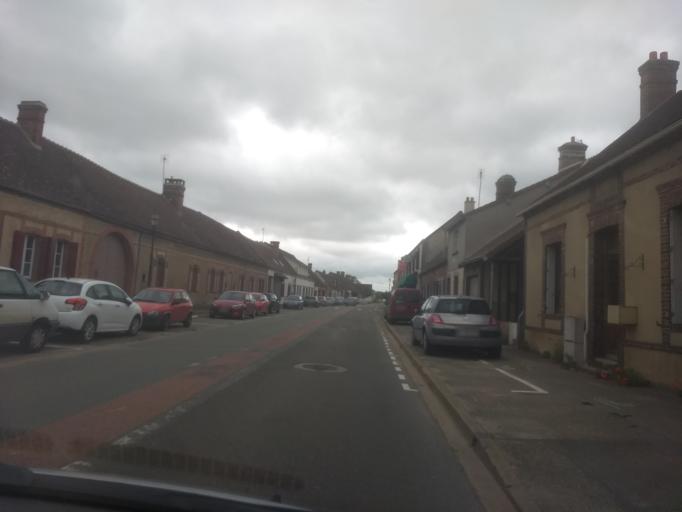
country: FR
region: Centre
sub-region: Departement d'Eure-et-Loir
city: Chateauneuf-en-Thymerais
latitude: 48.5360
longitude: 1.1539
